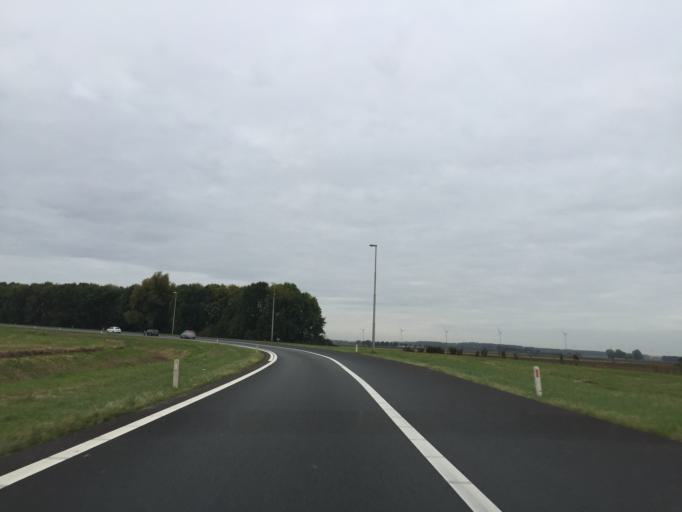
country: NL
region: North Brabant
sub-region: Gemeente Breda
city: Breda
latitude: 51.6472
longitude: 4.6883
